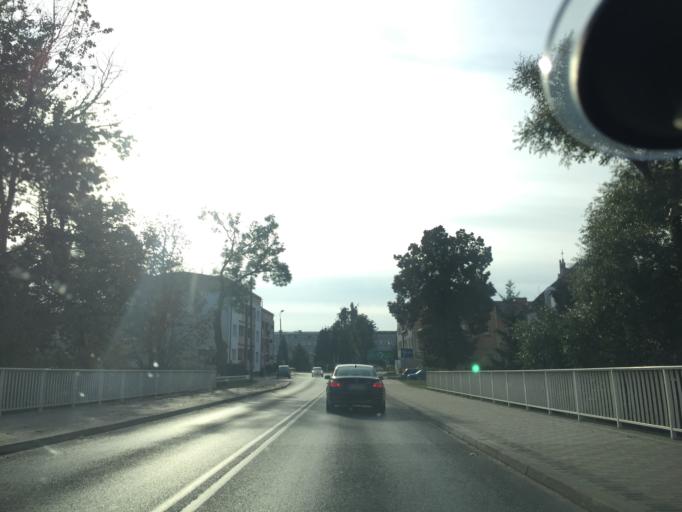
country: PL
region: Warmian-Masurian Voivodeship
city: Dobre Miasto
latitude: 53.9881
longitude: 20.3961
